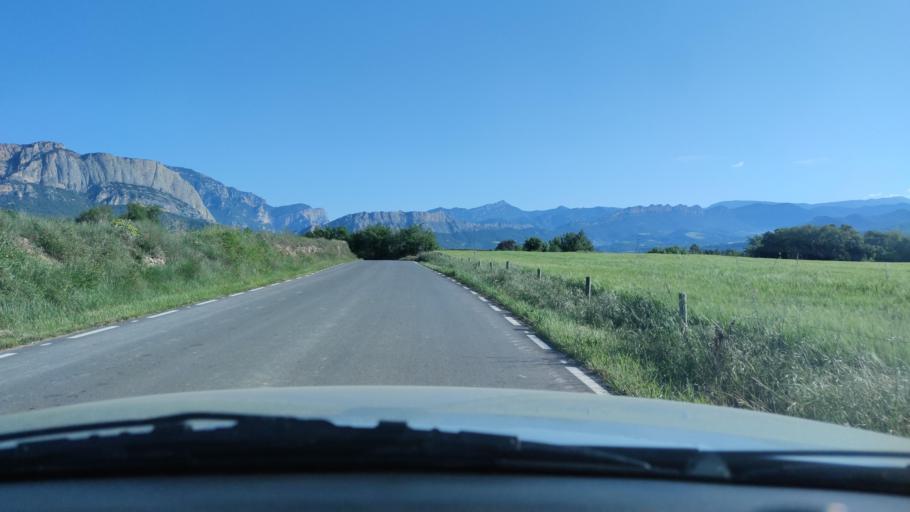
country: ES
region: Catalonia
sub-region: Provincia de Lleida
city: Oliana
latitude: 42.0469
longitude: 1.2929
